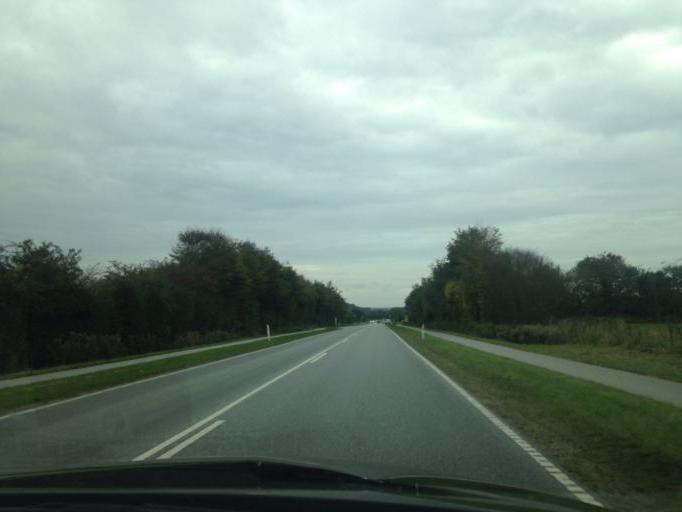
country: DK
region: South Denmark
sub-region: Haderslev Kommune
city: Haderslev
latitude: 55.2462
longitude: 9.4174
